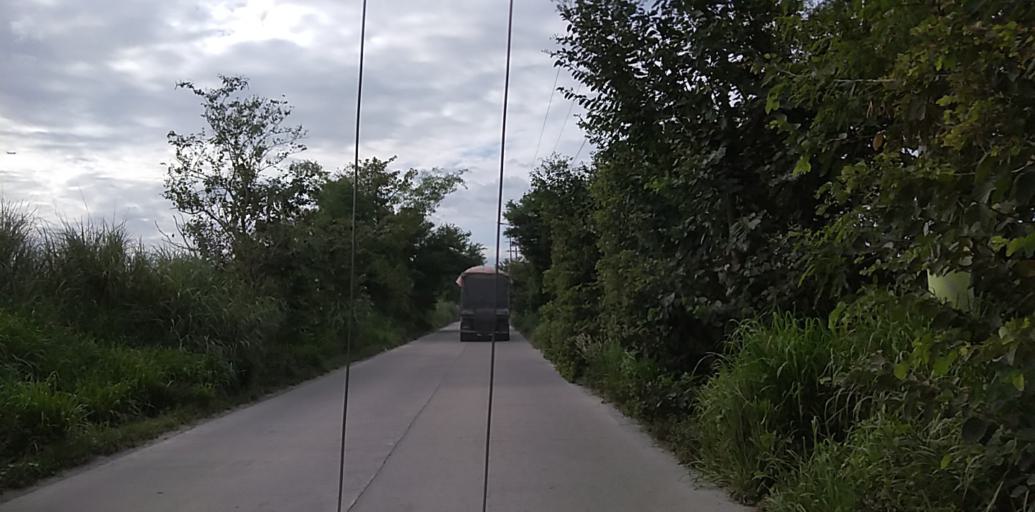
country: PH
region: Central Luzon
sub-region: Province of Pampanga
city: Porac
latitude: 15.0695
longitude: 120.5519
